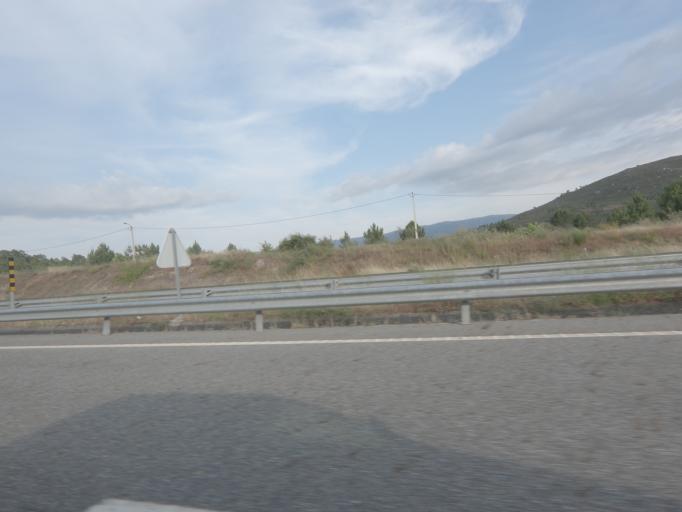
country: PT
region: Vila Real
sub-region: Boticas
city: Boticas
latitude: 41.6443
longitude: -7.5875
